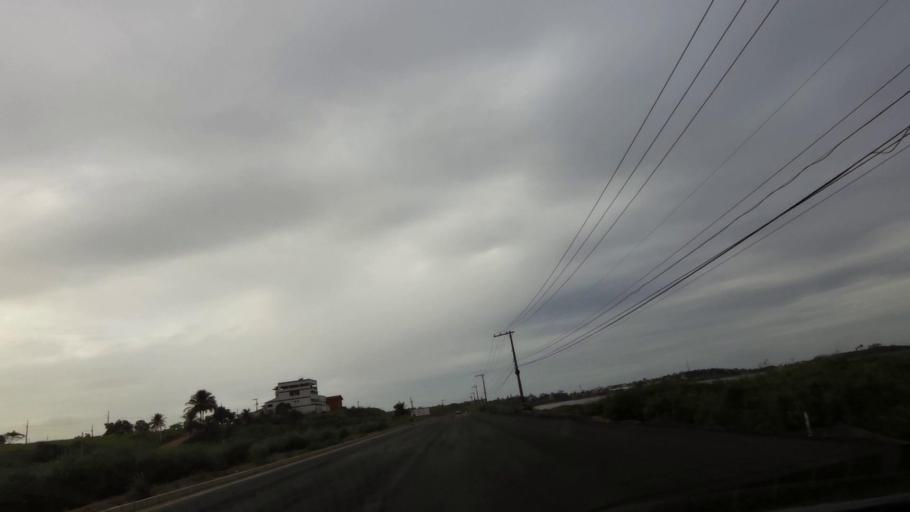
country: BR
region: Espirito Santo
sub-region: Guarapari
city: Guarapari
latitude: -20.7461
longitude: -40.5567
